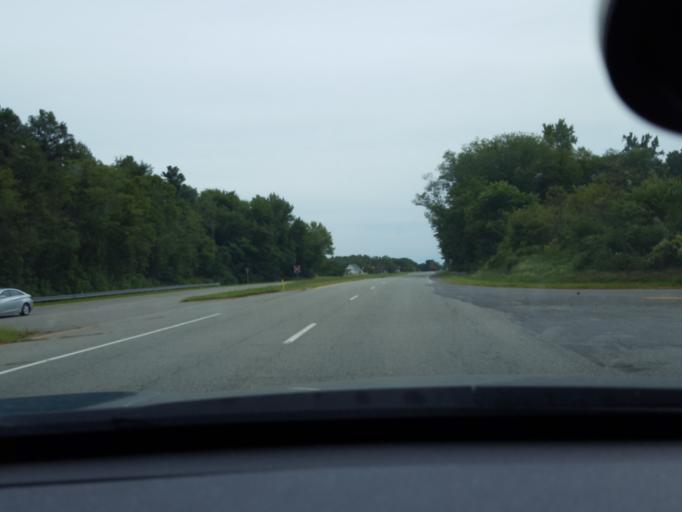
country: US
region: Virginia
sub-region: Caroline County
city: Bowling Green
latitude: 38.0292
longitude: -77.3405
